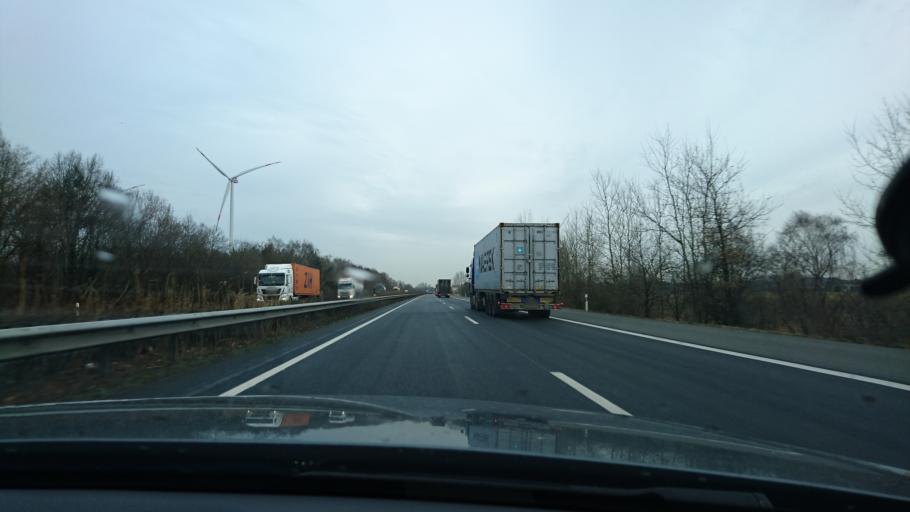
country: DE
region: Lower Saxony
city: Rieste
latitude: 52.4522
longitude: 8.0416
